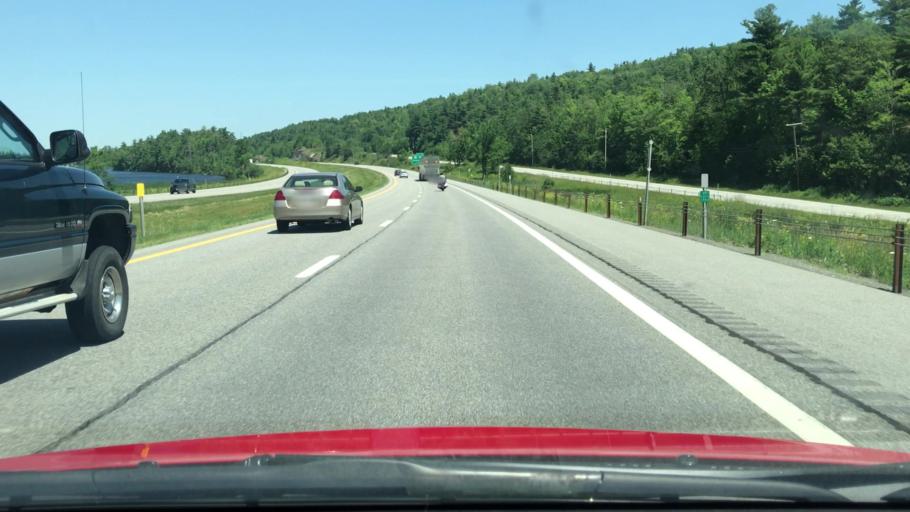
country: US
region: New York
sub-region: Essex County
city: Keeseville
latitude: 44.4227
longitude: -73.4938
